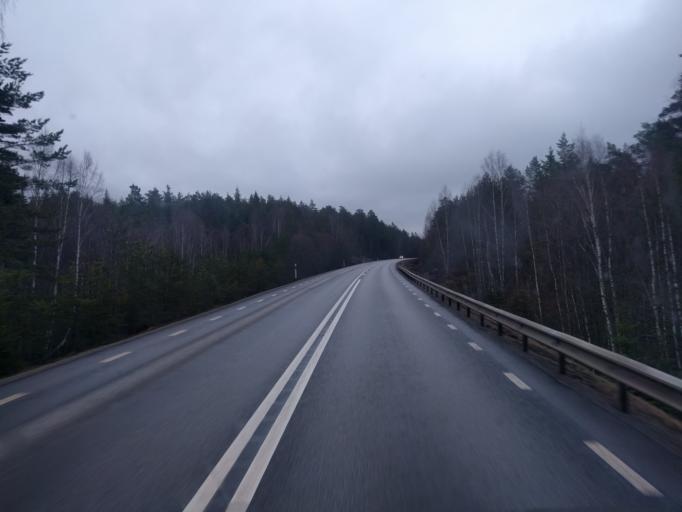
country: SE
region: Kalmar
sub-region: Vimmerby Kommun
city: Vimmerby
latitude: 57.6415
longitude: 15.7680
